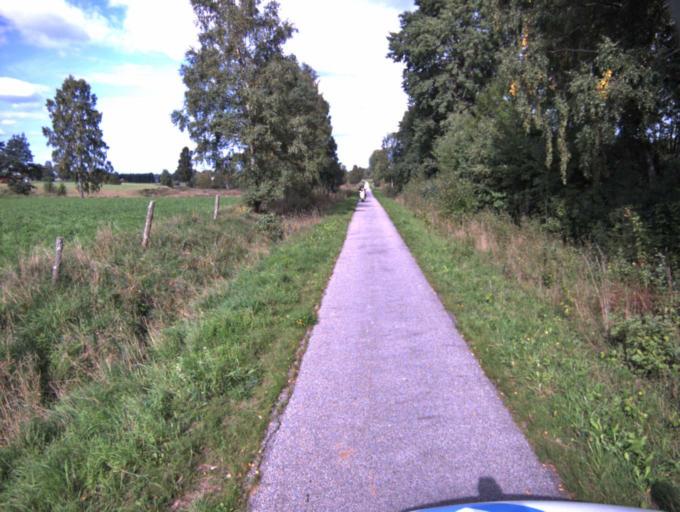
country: SE
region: Vaestra Goetaland
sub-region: Ulricehamns Kommun
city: Ulricehamn
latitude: 57.8495
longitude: 13.4252
